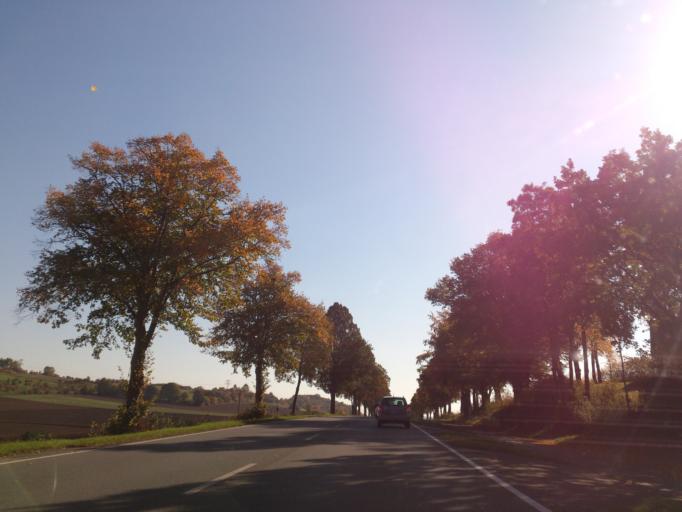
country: DE
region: North Rhine-Westphalia
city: Warburg
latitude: 51.5070
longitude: 9.0964
